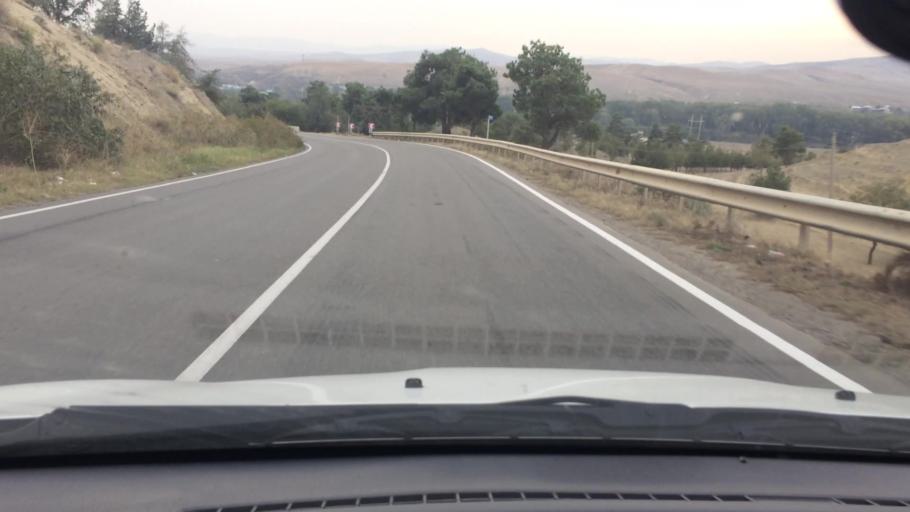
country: GE
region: Kvemo Kartli
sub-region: Gardabani
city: Gardabani
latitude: 41.3450
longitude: 45.0681
